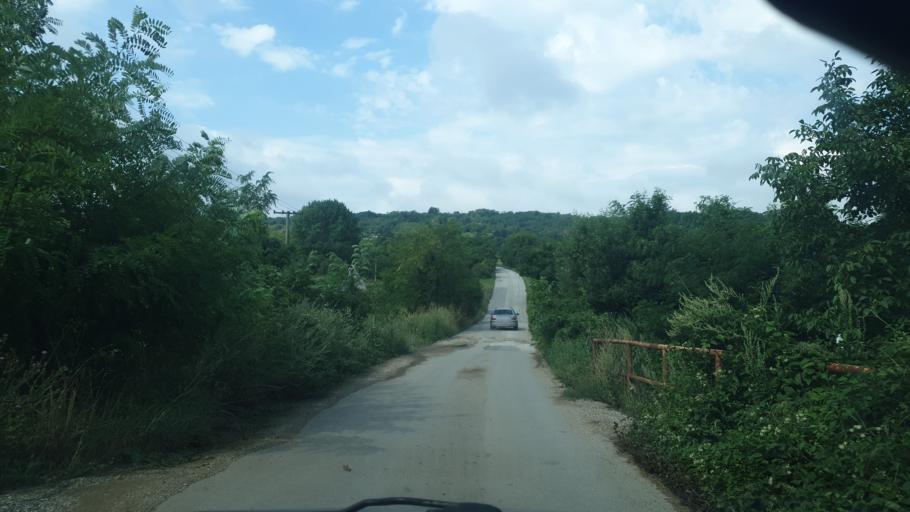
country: RS
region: Central Serbia
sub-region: Sumadijski Okrug
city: Kragujevac
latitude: 44.1047
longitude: 20.7861
